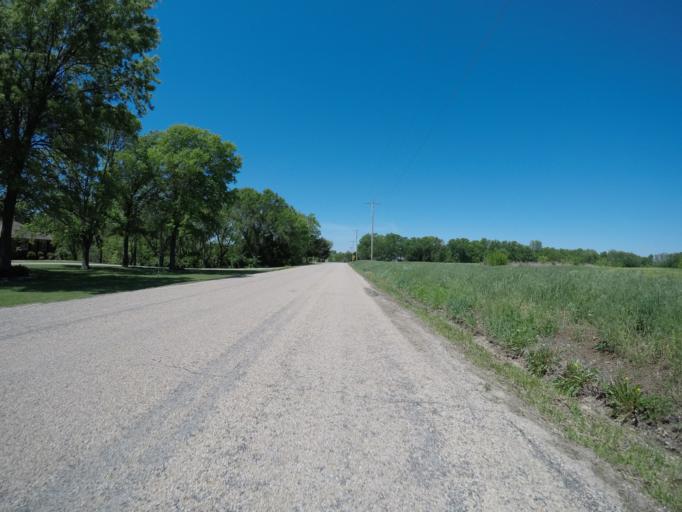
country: US
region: Kansas
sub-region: Shawnee County
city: Topeka
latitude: 39.0152
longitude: -95.5345
